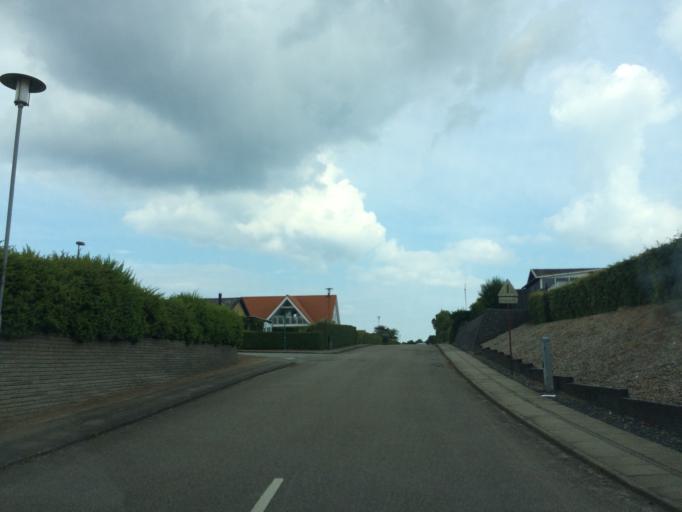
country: DK
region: South Denmark
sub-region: Middelfart Kommune
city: Strib
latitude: 55.5323
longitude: 9.7712
